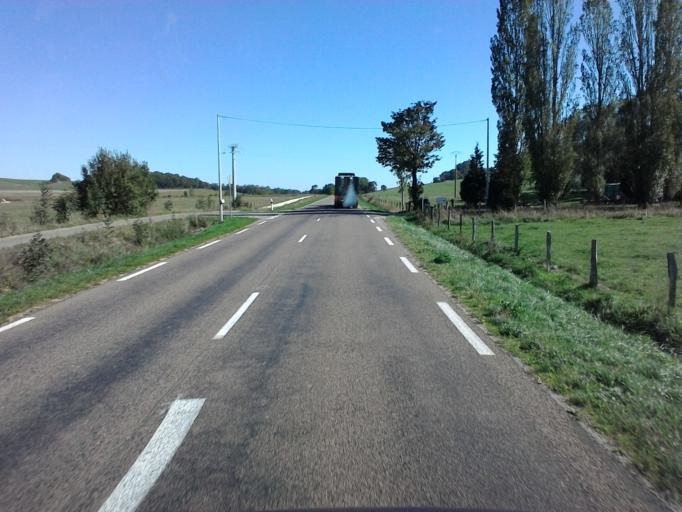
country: FR
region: Champagne-Ardenne
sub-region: Departement de la Haute-Marne
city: Lavilleneuve-au-Roi
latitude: 48.0920
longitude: 5.0223
